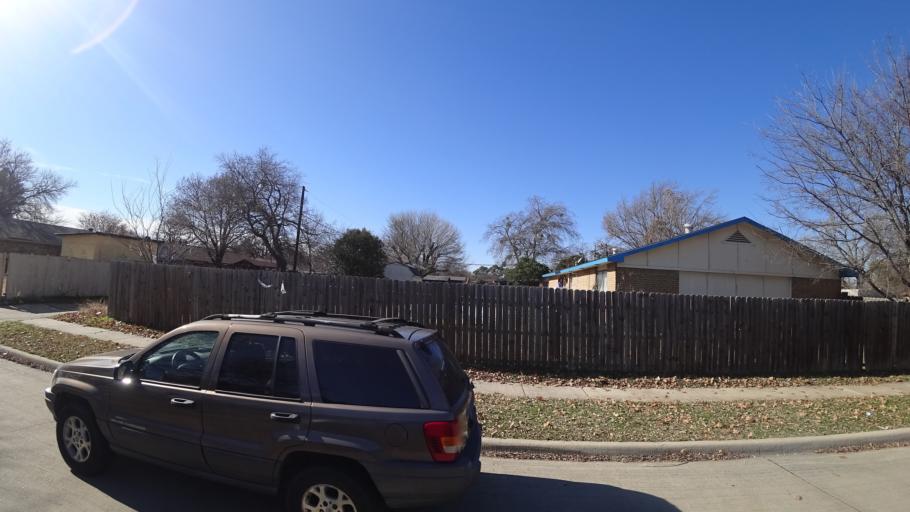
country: US
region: Texas
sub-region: Denton County
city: Lewisville
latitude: 33.0337
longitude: -97.0215
